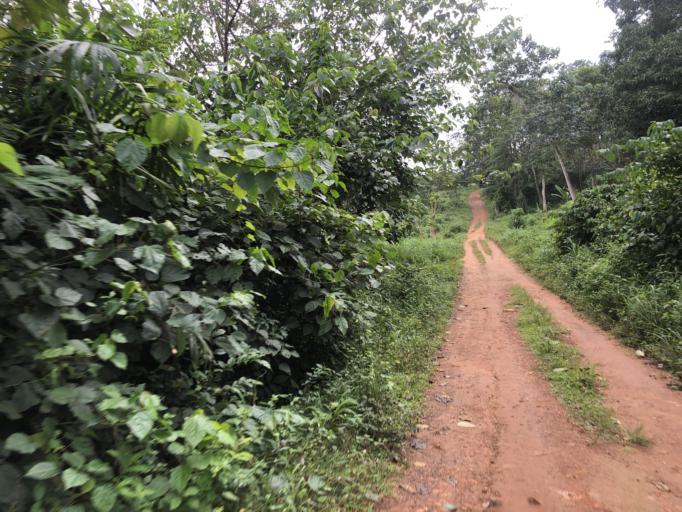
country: SL
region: Eastern Province
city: Kailahun
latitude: 8.2746
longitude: -10.5582
